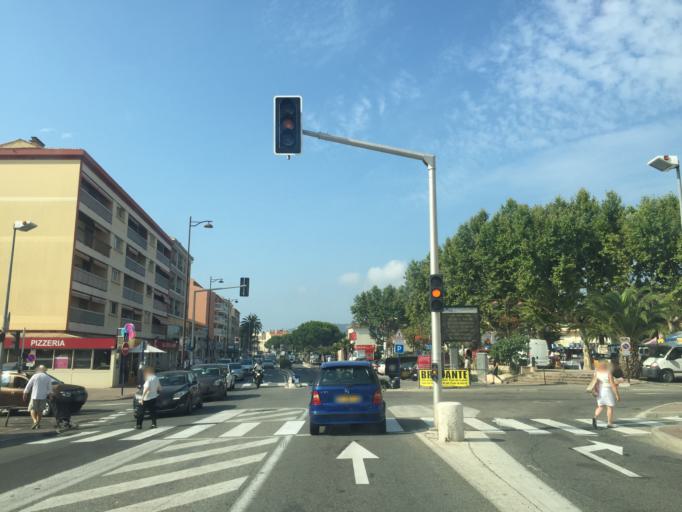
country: FR
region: Provence-Alpes-Cote d'Azur
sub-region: Departement du Var
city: Frejus
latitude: 43.3863
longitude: 6.7232
